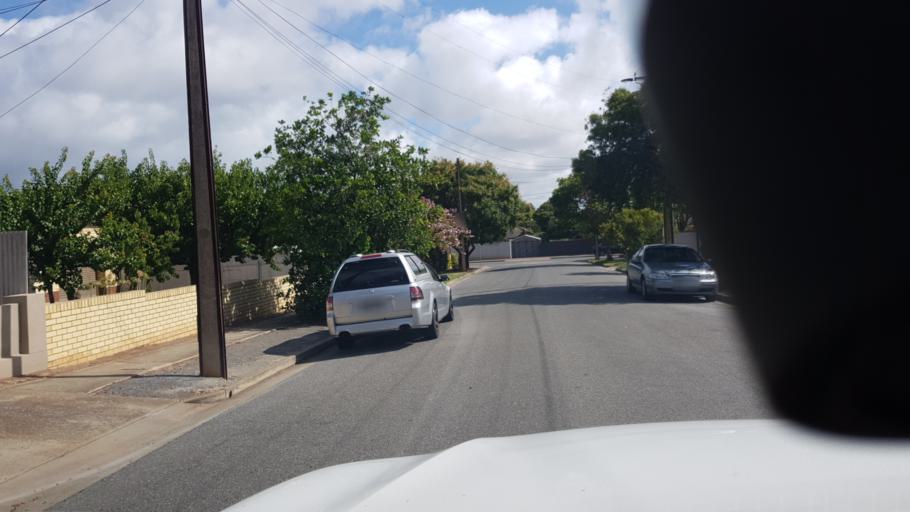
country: AU
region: South Australia
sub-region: Holdfast Bay
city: Seacliff Park
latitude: -35.0273
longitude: 138.5263
